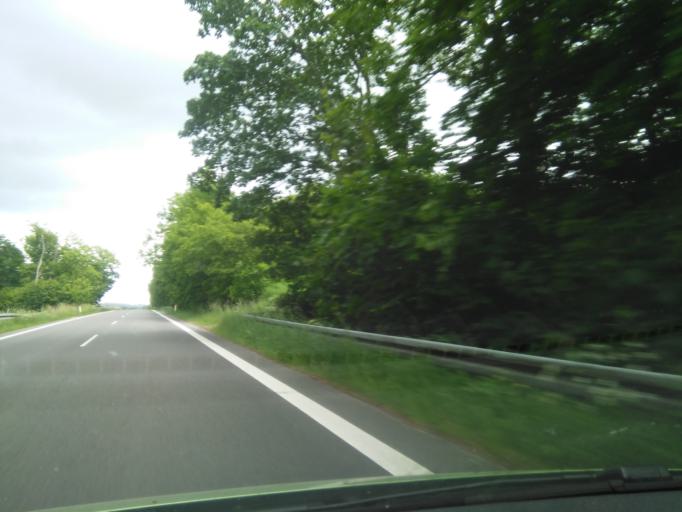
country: DK
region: Capital Region
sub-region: Bornholm Kommune
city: Akirkeby
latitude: 55.2204
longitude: 14.9081
